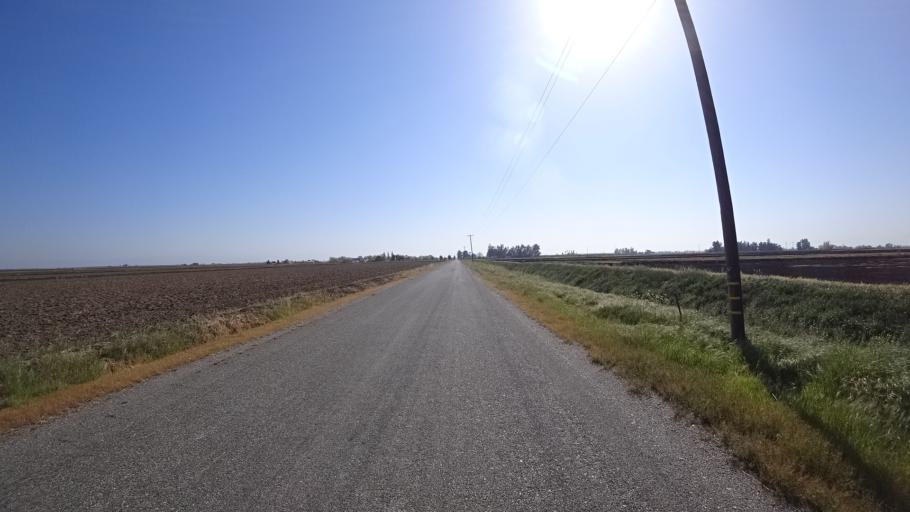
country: US
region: California
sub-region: Glenn County
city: Willows
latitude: 39.6018
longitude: -122.0693
